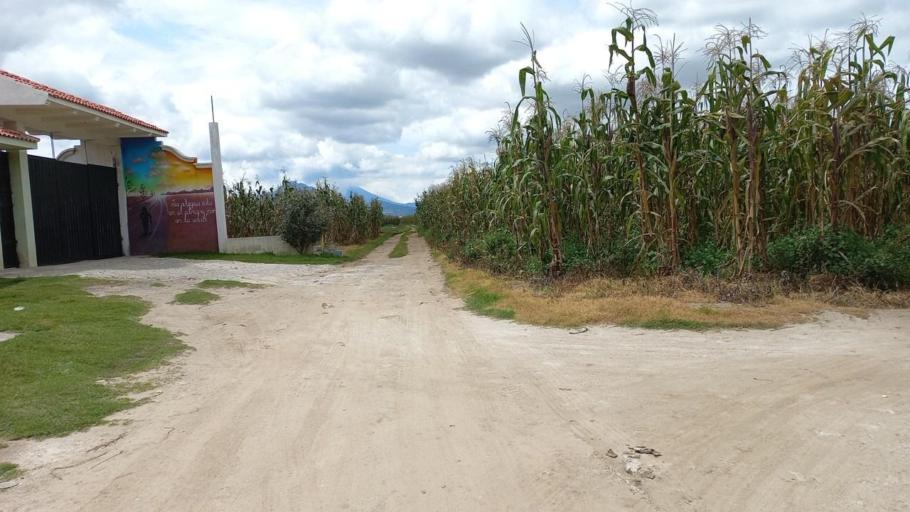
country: GT
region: Totonicapan
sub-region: Municipio de San Andres Xecul
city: San Andres Xecul
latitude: 14.8931
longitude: -91.4660
